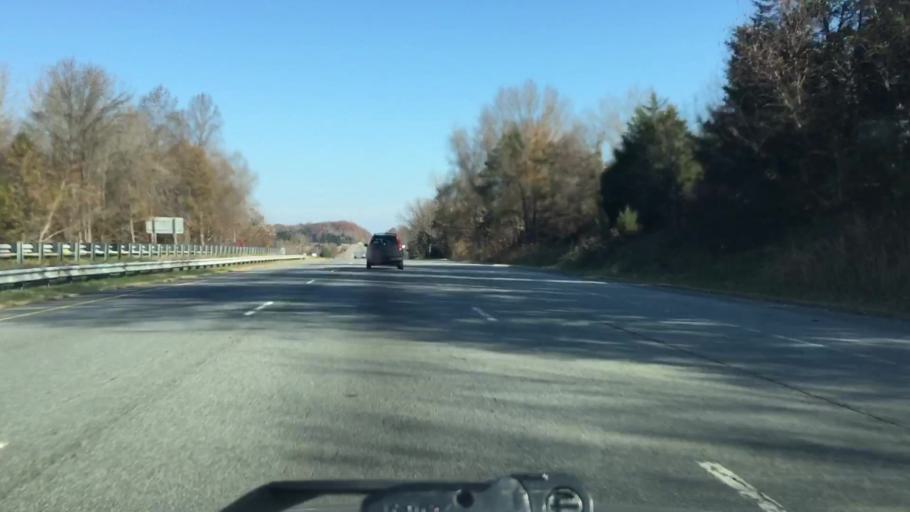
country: US
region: North Carolina
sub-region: Guilford County
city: McLeansville
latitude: 36.1764
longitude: -79.7115
